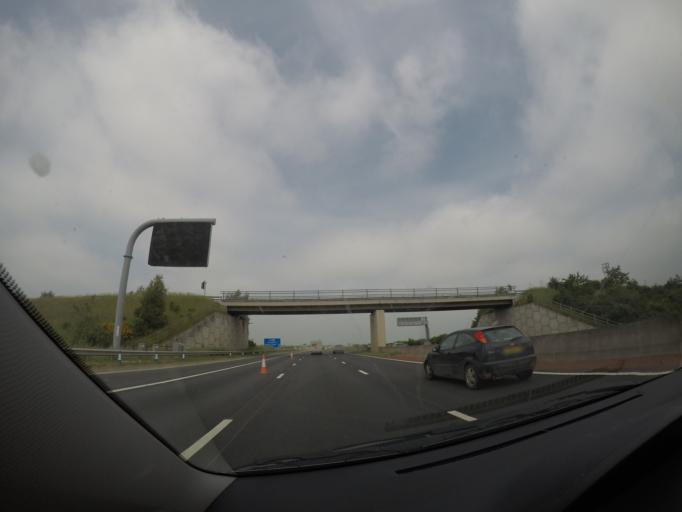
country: GB
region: England
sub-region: North Yorkshire
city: Ripon
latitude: 54.1641
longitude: -1.4483
